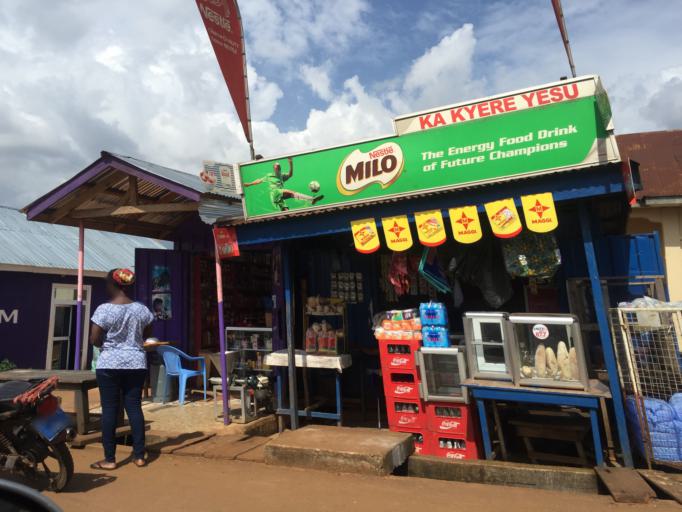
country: GH
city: Mpraeso
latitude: 6.5860
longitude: -0.7366
